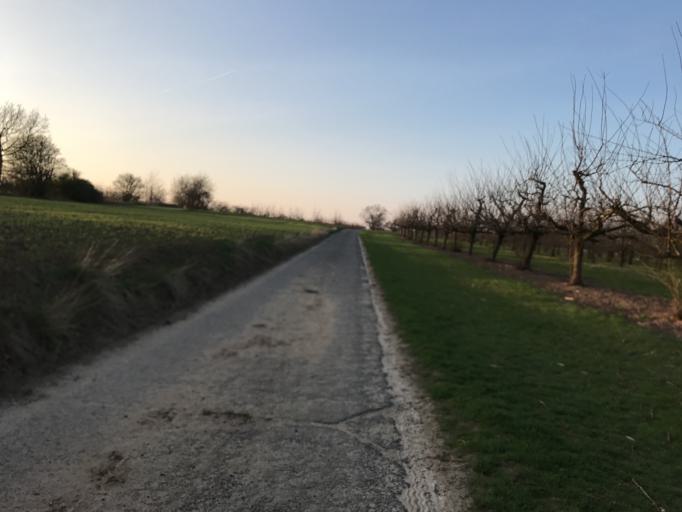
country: DE
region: Rheinland-Pfalz
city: Ober-Olm
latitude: 49.9659
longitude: 8.1956
